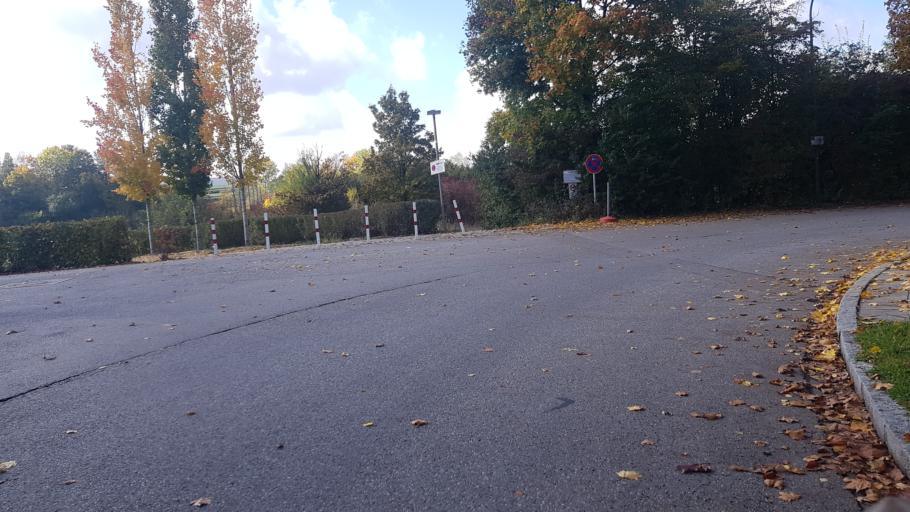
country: DE
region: Bavaria
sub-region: Upper Bavaria
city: Neuried
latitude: 48.1123
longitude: 11.4649
